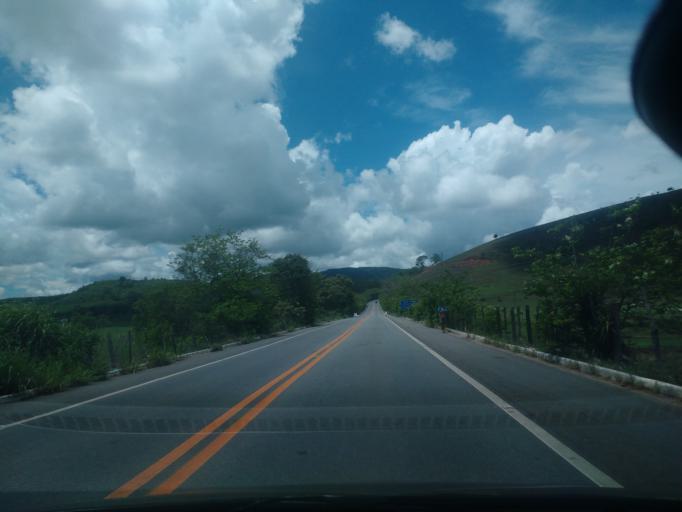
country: BR
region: Alagoas
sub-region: Uniao Dos Palmares
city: Uniao dos Palmares
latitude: -9.1352
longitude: -36.0234
